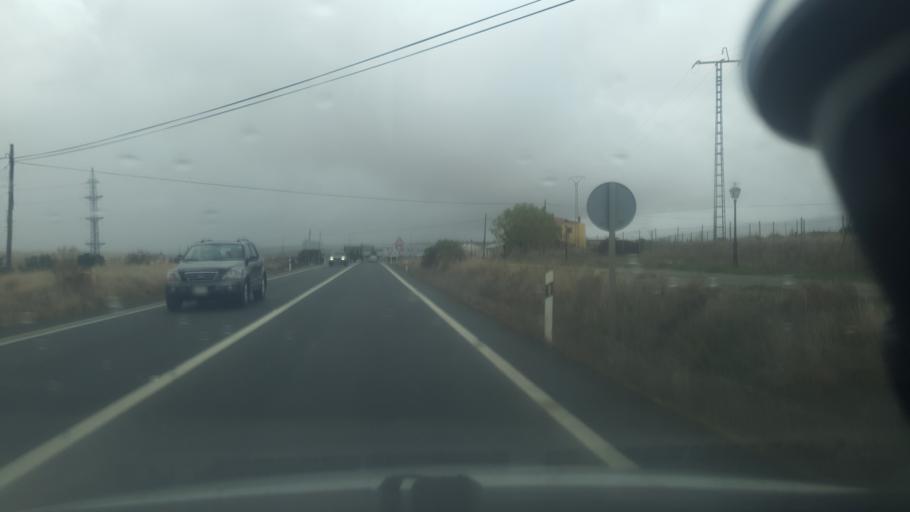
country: ES
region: Castille and Leon
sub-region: Provincia de Segovia
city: Villacastin
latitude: 40.7798
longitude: -4.4222
